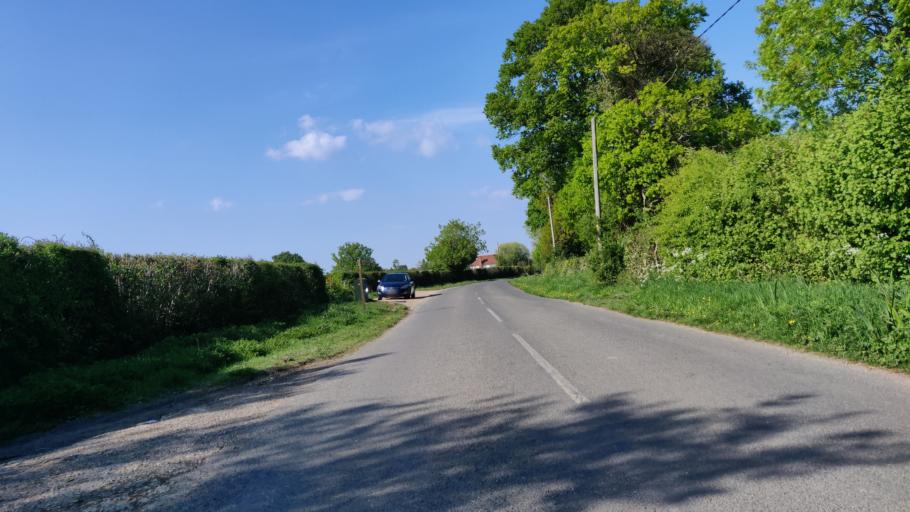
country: GB
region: England
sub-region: West Sussex
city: Southwater
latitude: 51.0392
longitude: -0.3580
